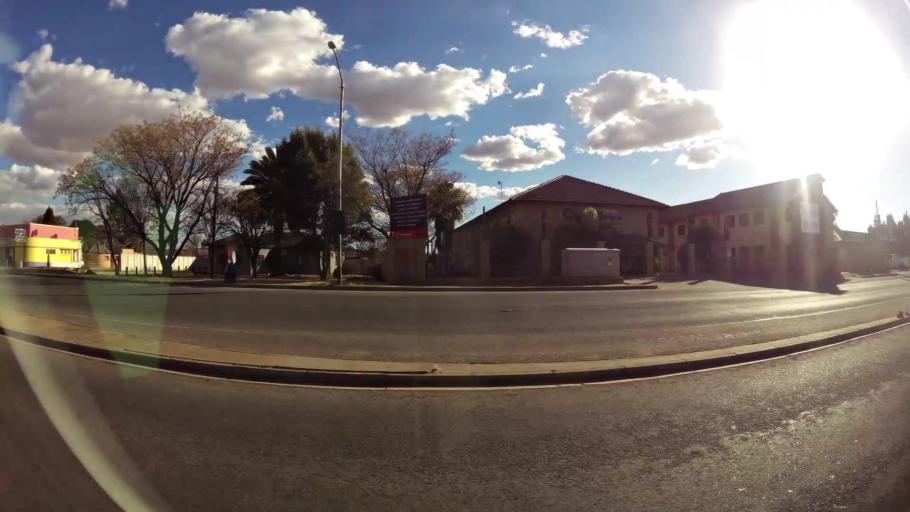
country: ZA
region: North-West
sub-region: Dr Kenneth Kaunda District Municipality
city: Klerksdorp
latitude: -26.8533
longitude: 26.6645
